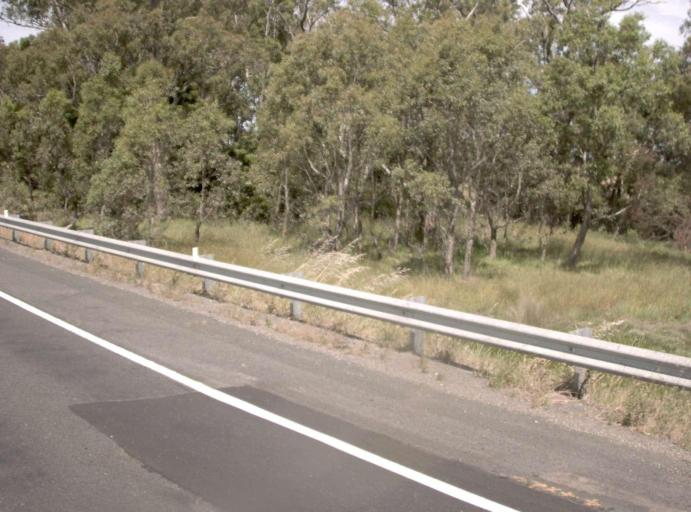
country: AU
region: Victoria
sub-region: East Gippsland
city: Bairnsdale
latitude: -37.8960
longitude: 147.3694
